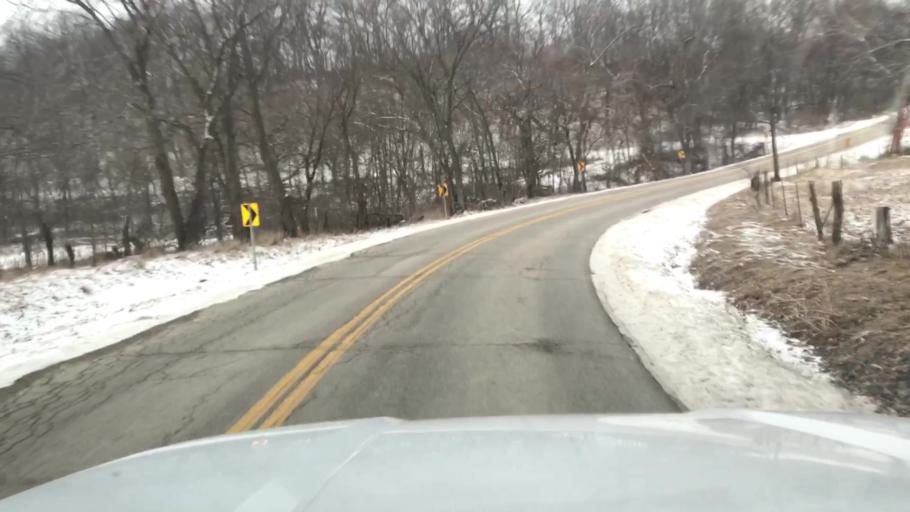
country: US
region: Missouri
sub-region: Andrew County
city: Savannah
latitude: 40.0237
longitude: -94.9151
